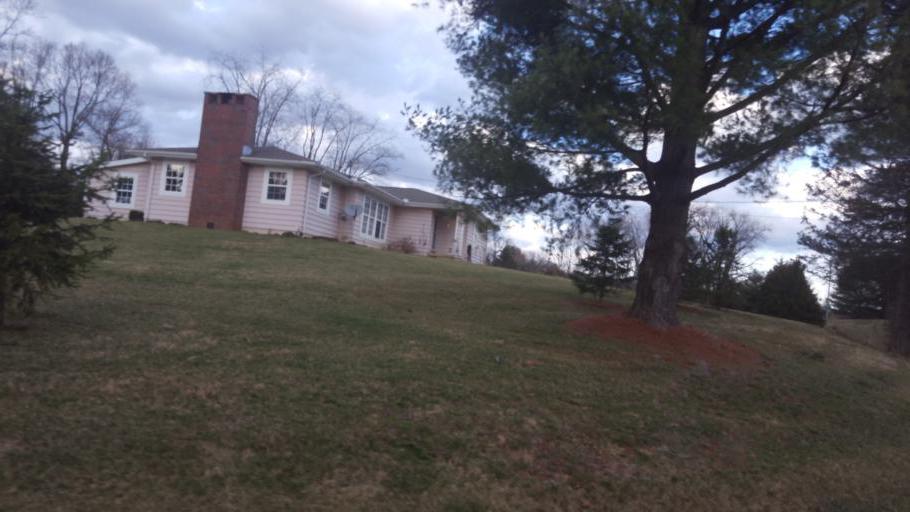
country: US
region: Ohio
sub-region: Knox County
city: Fredericktown
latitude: 40.4929
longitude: -82.5227
